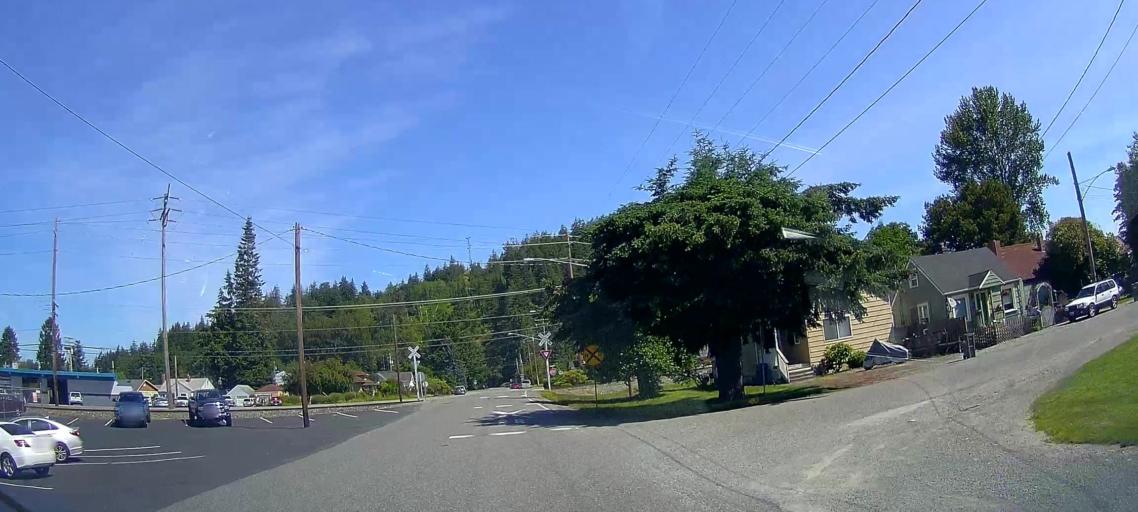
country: US
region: Washington
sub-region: Skagit County
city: Burlington
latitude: 48.4762
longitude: -122.3247
